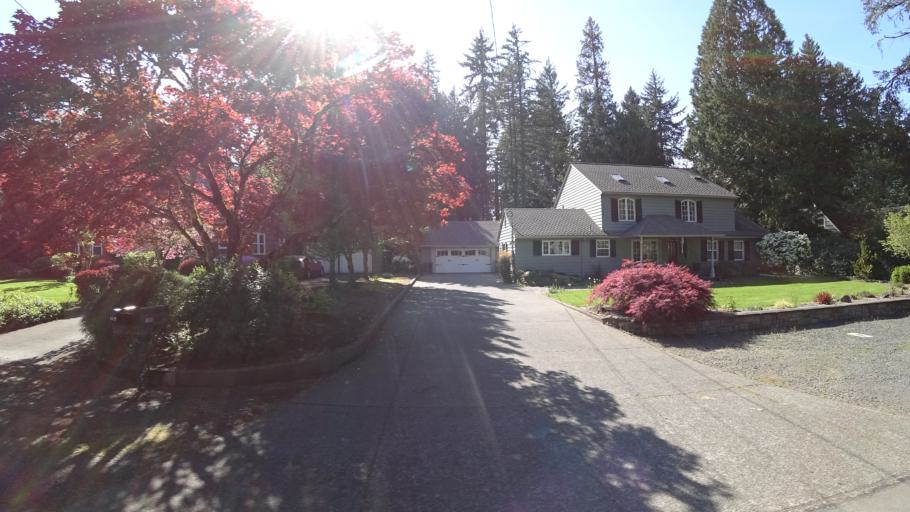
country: US
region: Oregon
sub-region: Washington County
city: Hillsboro
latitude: 45.5330
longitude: -122.9858
